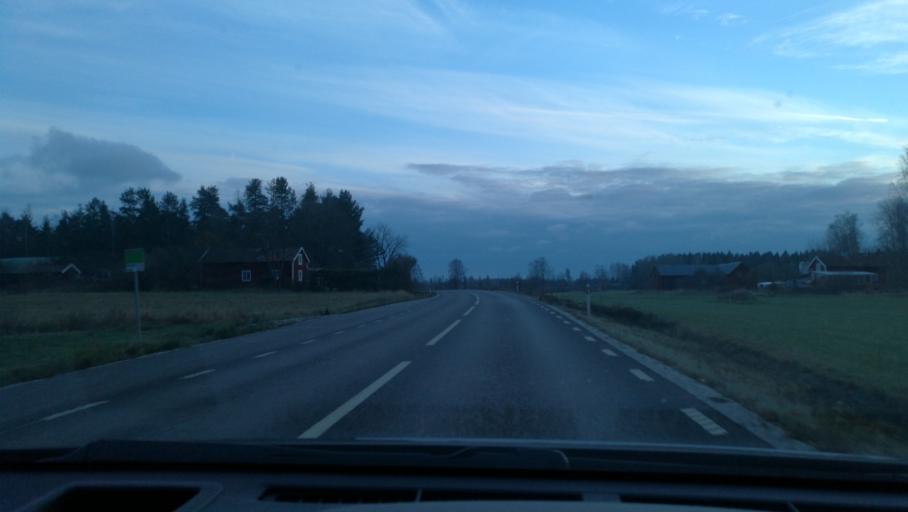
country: SE
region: Soedermanland
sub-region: Vingakers Kommun
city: Vingaker
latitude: 59.1116
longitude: 15.8177
